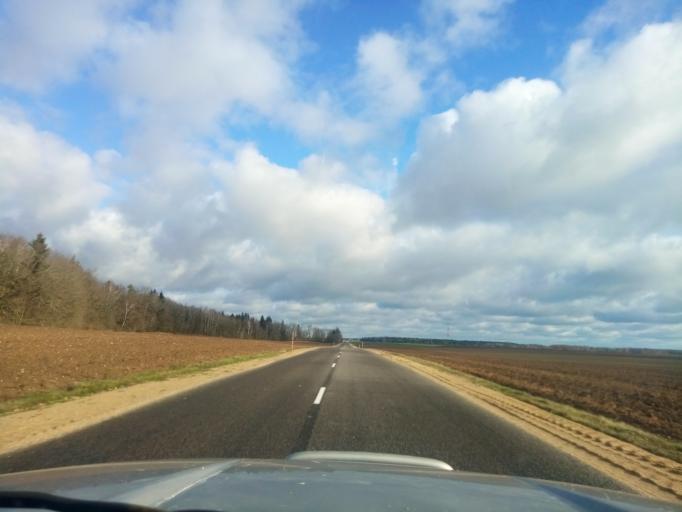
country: BY
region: Minsk
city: Tsimkavichy
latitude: 53.1398
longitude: 27.0104
